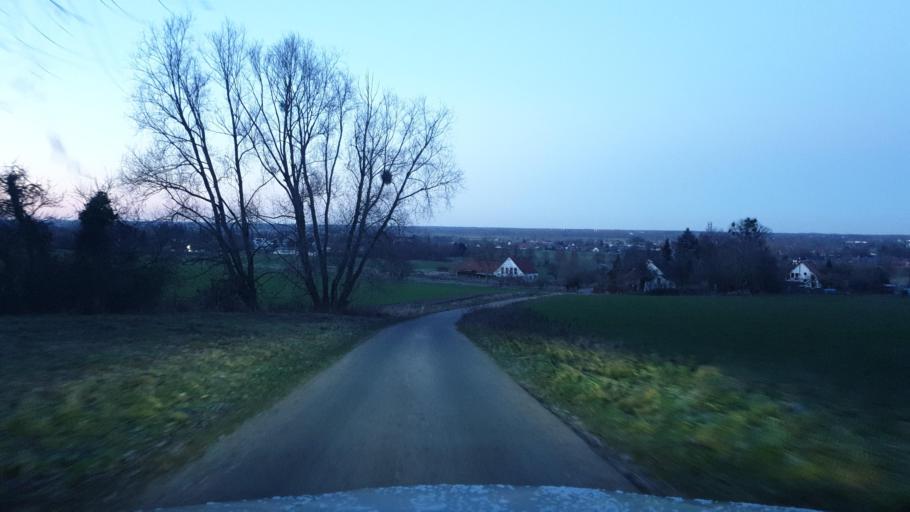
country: DE
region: North Rhine-Westphalia
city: Porta Westfalica
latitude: 52.2582
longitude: 8.8570
